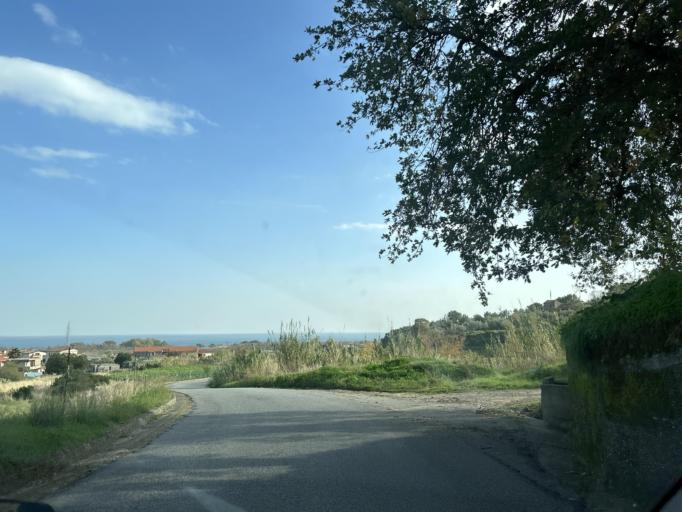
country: IT
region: Calabria
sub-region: Provincia di Catanzaro
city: Montepaone
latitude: 38.7161
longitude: 16.5209
